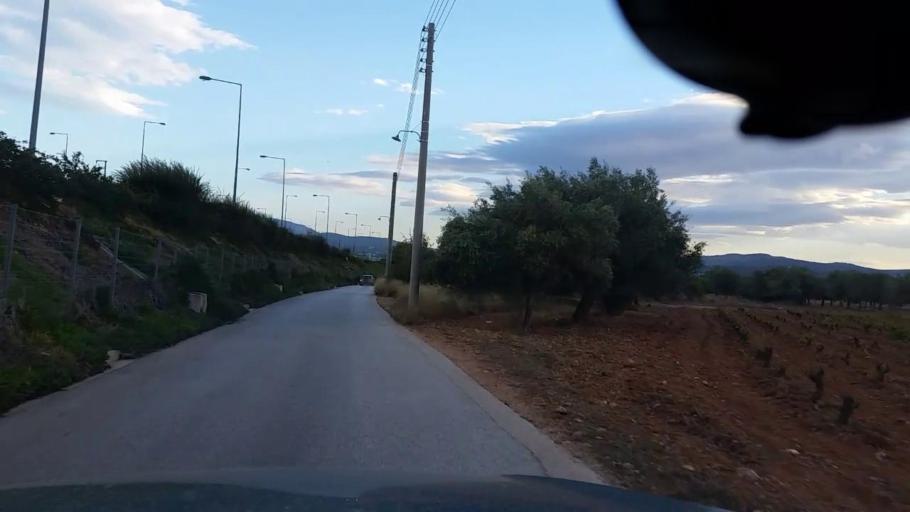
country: GR
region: Attica
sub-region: Nomarchia Anatolikis Attikis
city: Argithea
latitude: 37.9518
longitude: 23.8857
